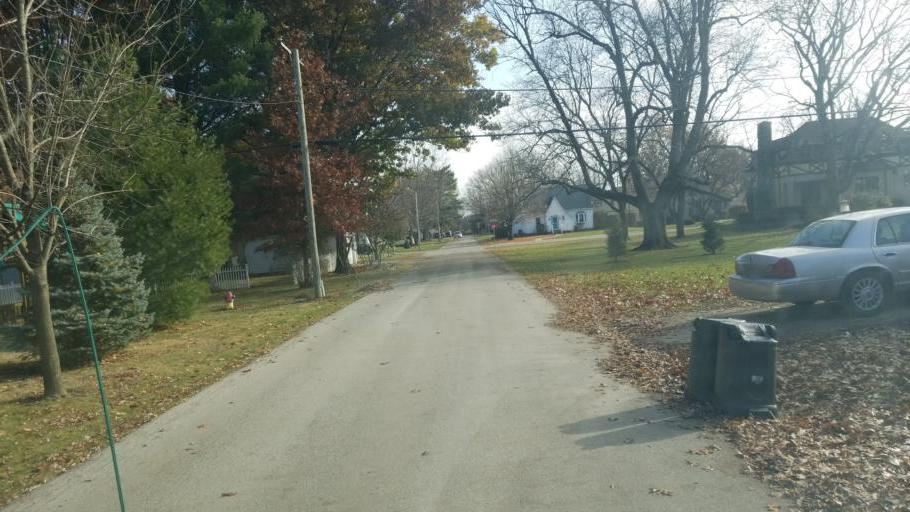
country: US
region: Indiana
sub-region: Adams County
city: Berne
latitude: 40.6517
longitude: -84.9535
